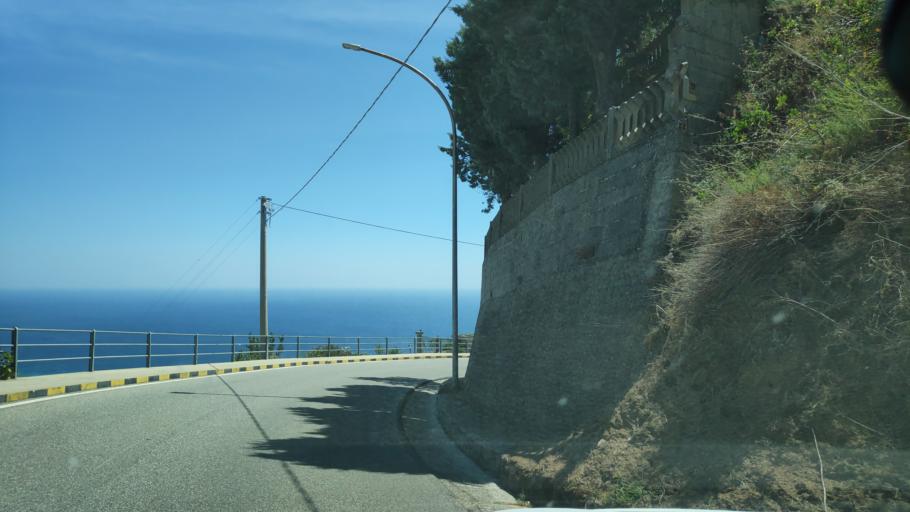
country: IT
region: Calabria
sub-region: Provincia di Catanzaro
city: Gasperina
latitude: 38.7381
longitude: 16.5116
